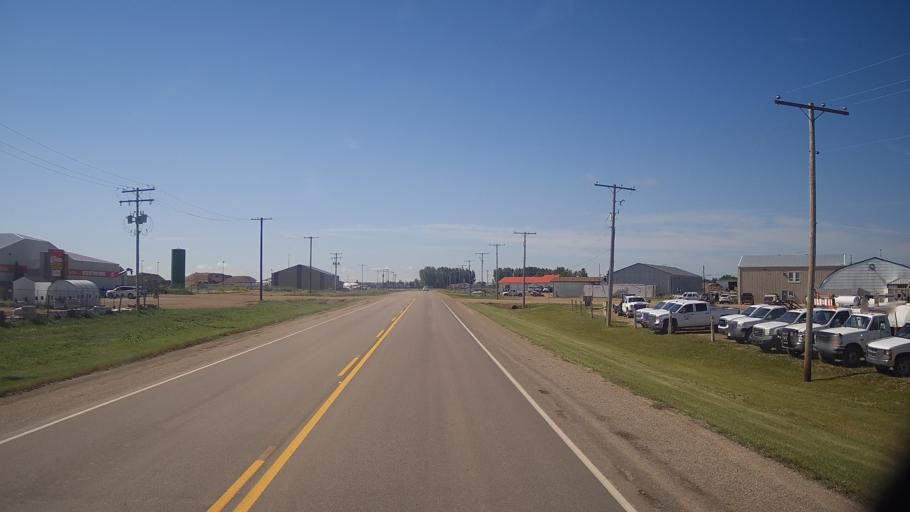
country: CA
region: Saskatchewan
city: Watrous
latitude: 51.6705
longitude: -105.4517
